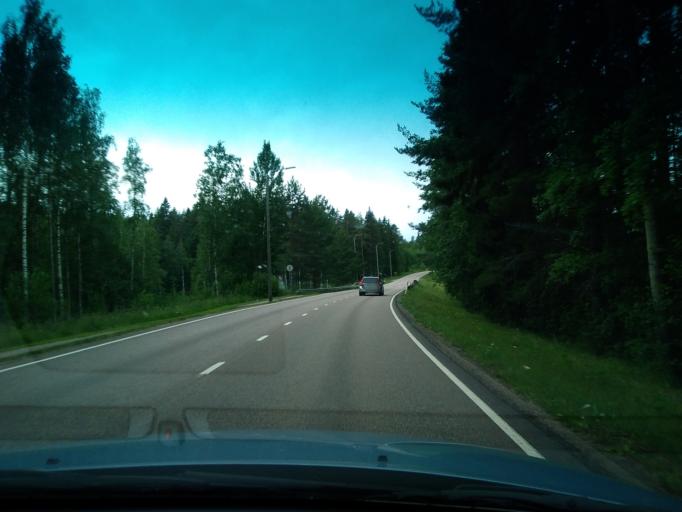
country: FI
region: Central Finland
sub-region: Keuruu
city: Multia
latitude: 62.4002
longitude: 24.7915
